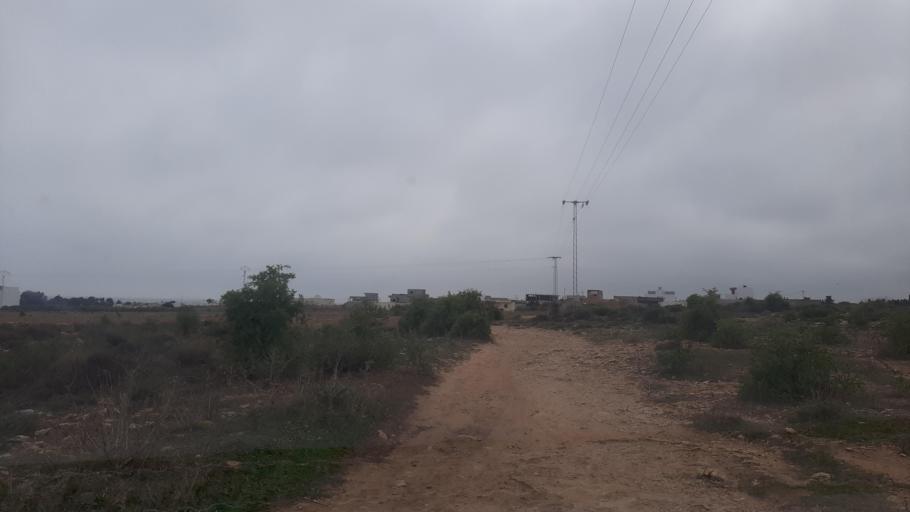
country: TN
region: Nabul
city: Menzel Heurr
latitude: 36.6868
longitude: 10.9311
